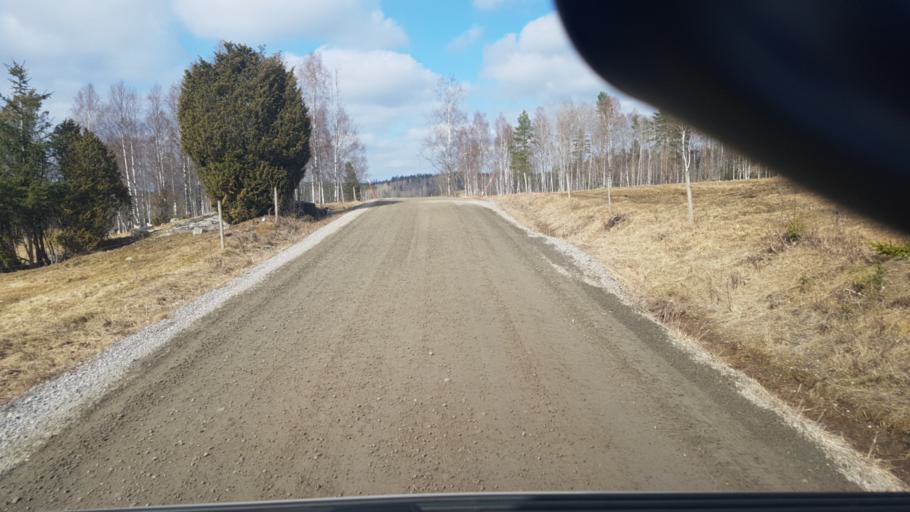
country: SE
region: Vaermland
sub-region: Eda Kommun
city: Amotfors
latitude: 59.7819
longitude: 12.4371
